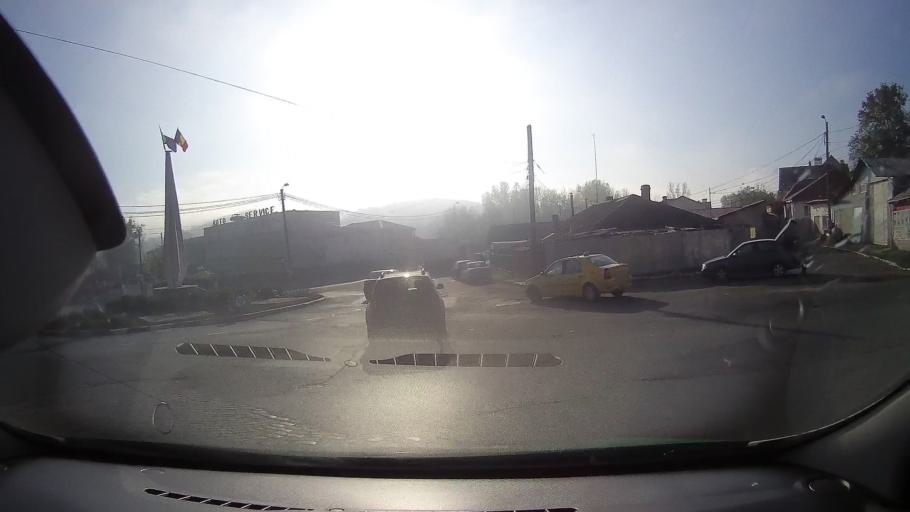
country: RO
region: Tulcea
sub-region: Municipiul Tulcea
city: Tulcea
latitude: 45.1658
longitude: 28.8166
